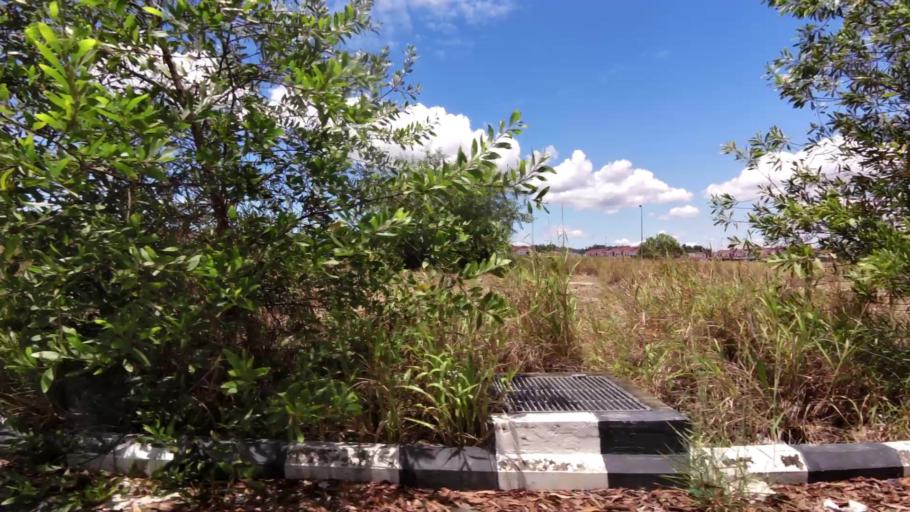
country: BN
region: Brunei and Muara
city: Bandar Seri Begawan
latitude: 5.0098
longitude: 115.0084
